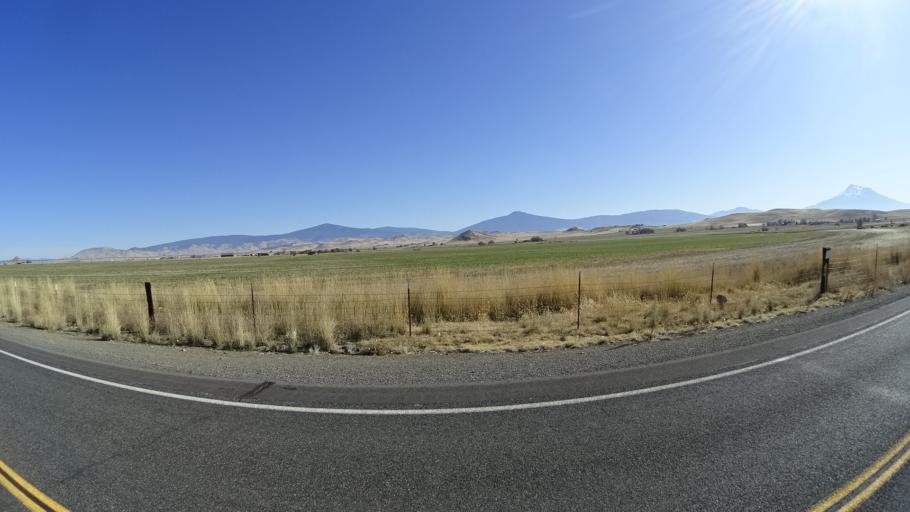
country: US
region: California
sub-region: Siskiyou County
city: Montague
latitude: 41.7516
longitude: -122.5247
